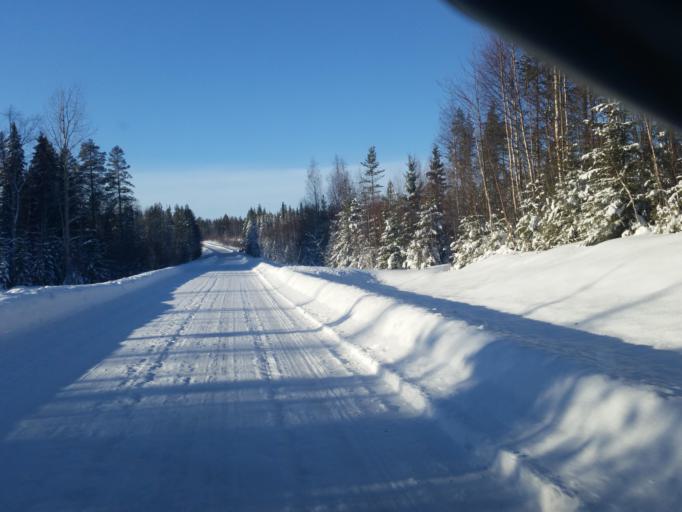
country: SE
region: Norrbotten
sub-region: Pitea Kommun
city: Hortlax
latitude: 65.2197
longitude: 21.2653
